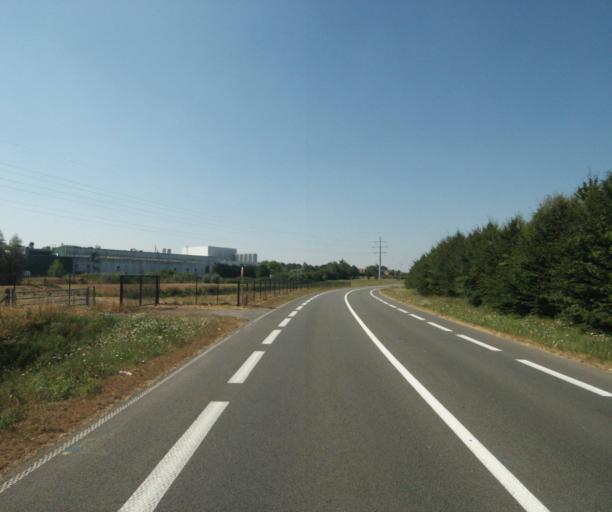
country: FR
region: Nord-Pas-de-Calais
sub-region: Departement du Nord
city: Bousbecque
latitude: 50.7679
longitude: 3.0906
